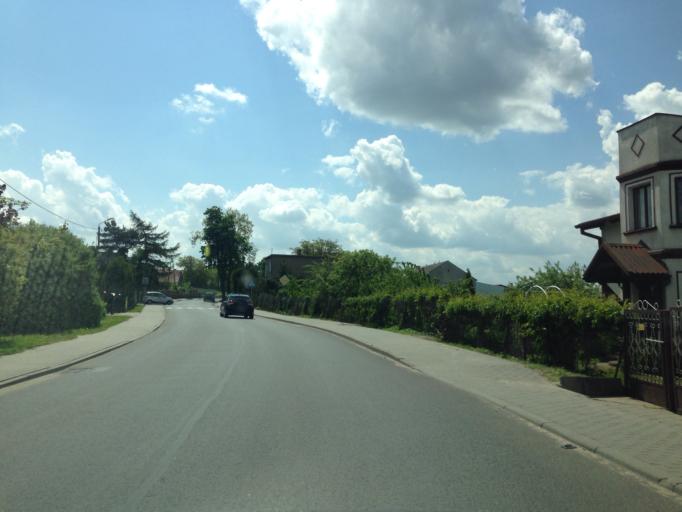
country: PL
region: Kujawsko-Pomorskie
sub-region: Powiat brodnicki
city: Brodnica
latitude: 53.3319
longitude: 19.3747
